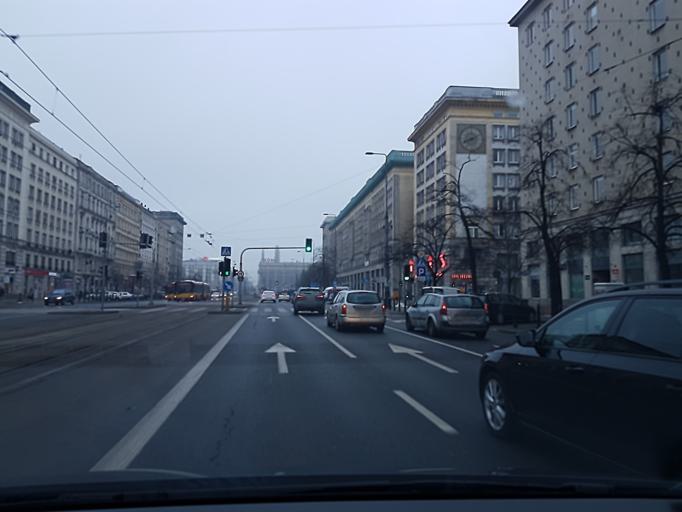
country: PL
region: Masovian Voivodeship
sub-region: Warszawa
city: Srodmiescie
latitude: 52.2252
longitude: 21.0143
